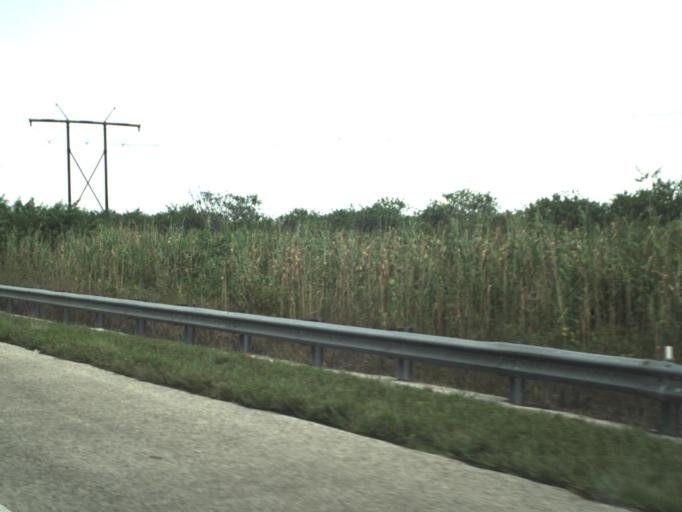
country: US
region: Florida
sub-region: Broward County
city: Weston
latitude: 26.3152
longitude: -80.5225
